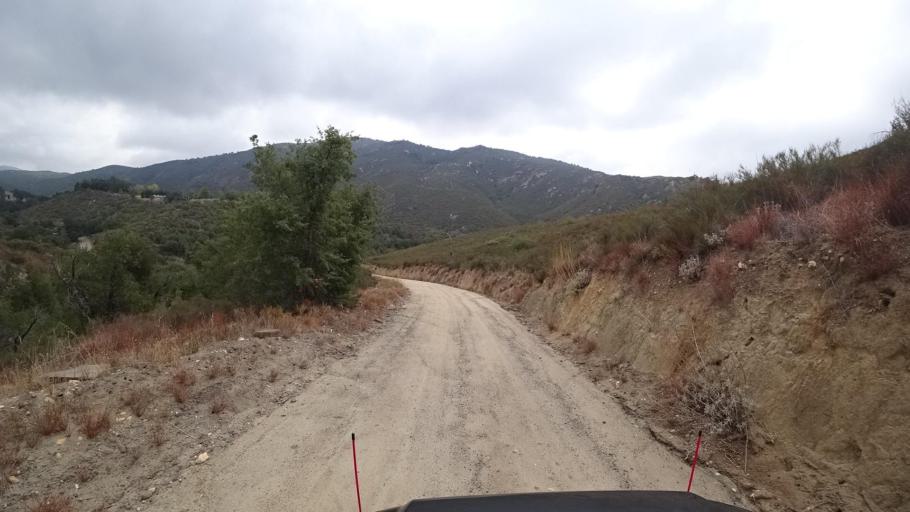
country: US
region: California
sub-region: San Diego County
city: San Diego Country Estates
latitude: 32.9715
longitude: -116.6731
